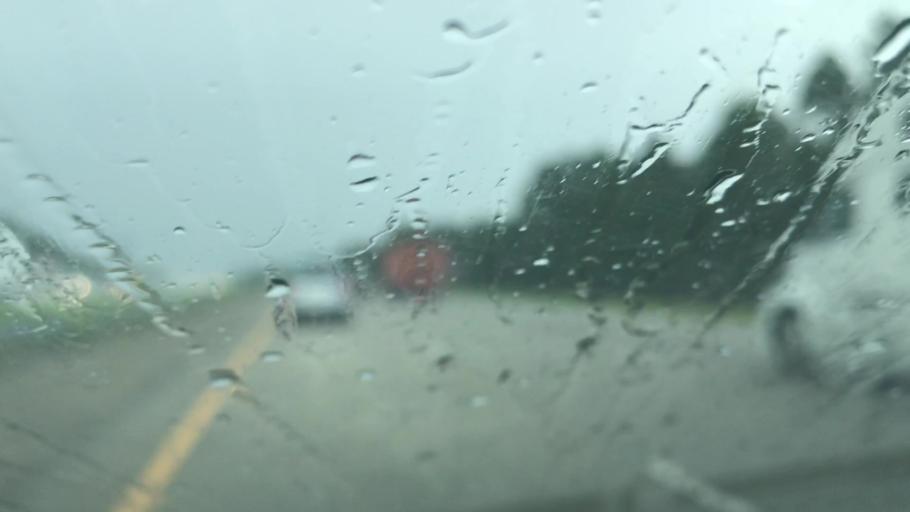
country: US
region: Georgia
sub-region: McIntosh County
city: Darien
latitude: 31.3208
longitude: -81.4749
